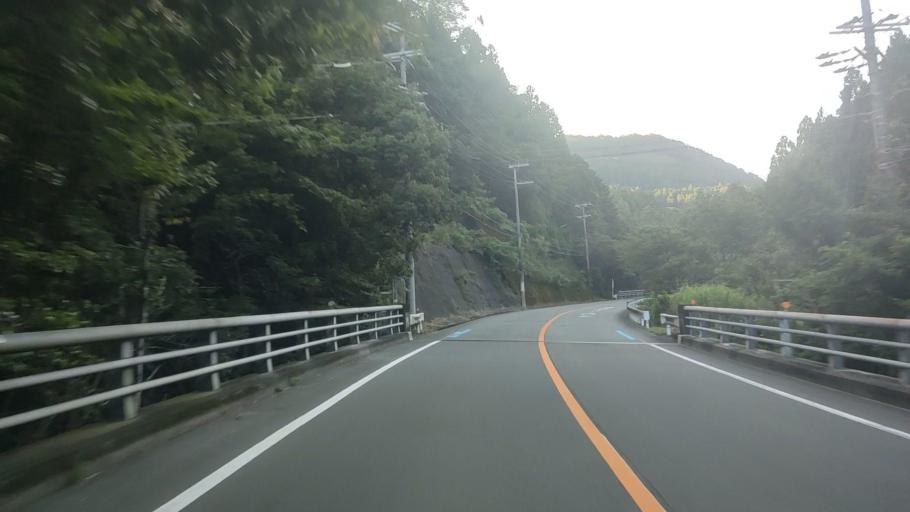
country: JP
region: Wakayama
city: Tanabe
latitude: 33.8159
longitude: 135.6165
